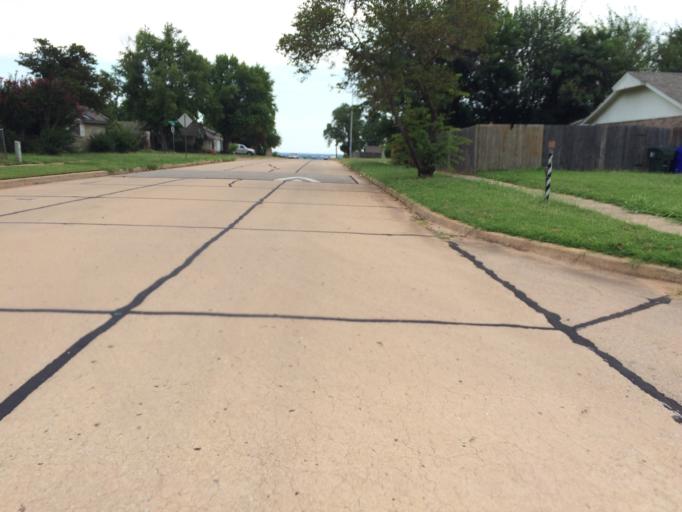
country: US
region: Oklahoma
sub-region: Cleveland County
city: Hall Park
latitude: 35.2522
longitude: -97.4191
